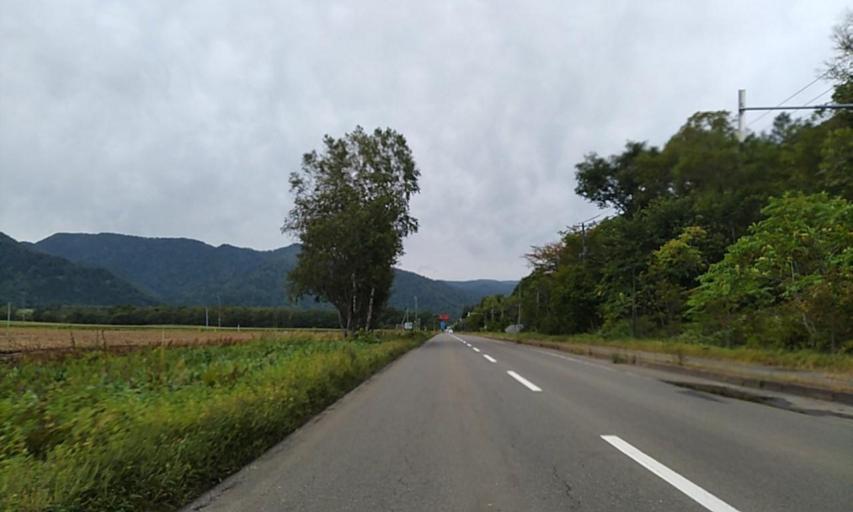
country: JP
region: Hokkaido
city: Bihoro
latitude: 43.5548
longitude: 144.3487
